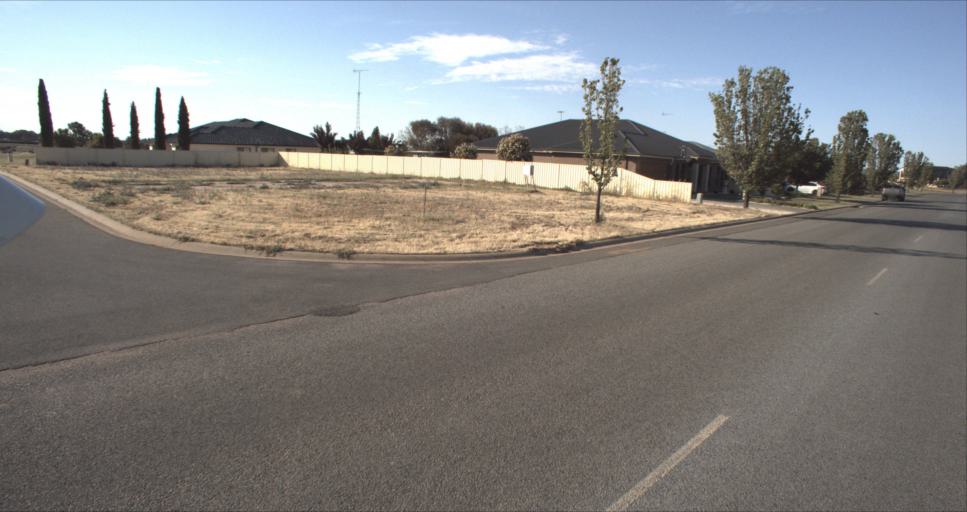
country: AU
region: New South Wales
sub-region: Leeton
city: Leeton
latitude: -34.5401
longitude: 146.4018
